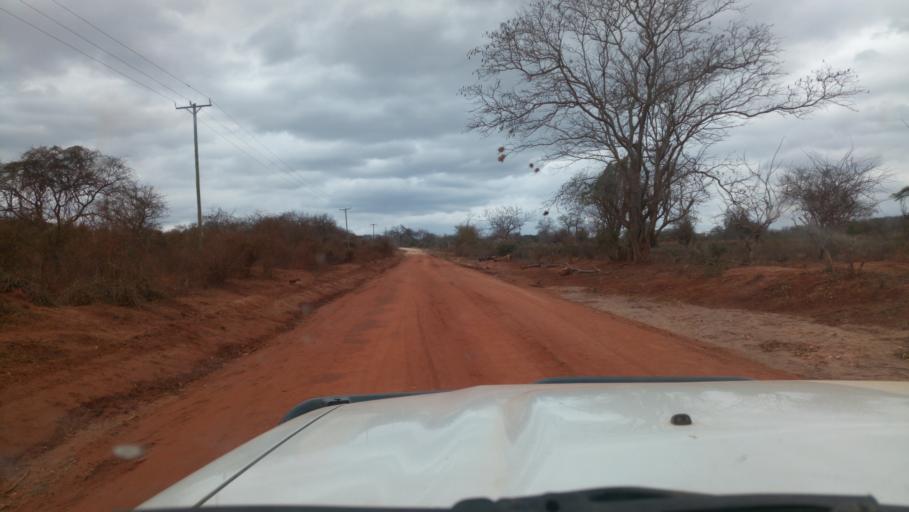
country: KE
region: Kitui
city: Kitui
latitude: -1.9636
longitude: 38.3598
